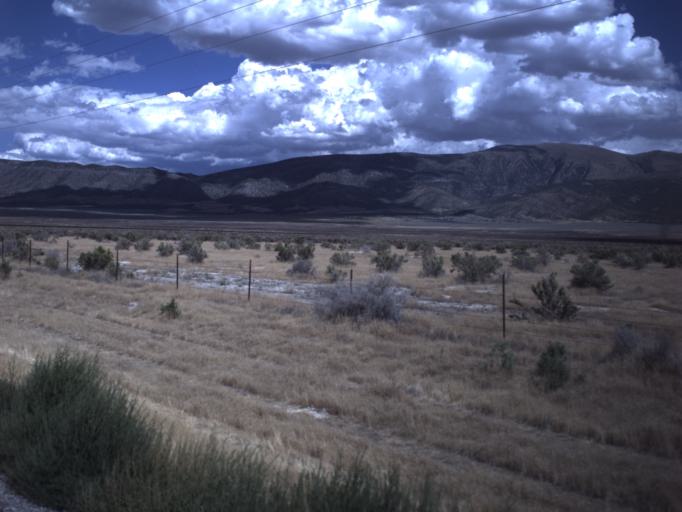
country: US
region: Utah
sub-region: Tooele County
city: Grantsville
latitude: 40.2666
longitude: -112.6858
